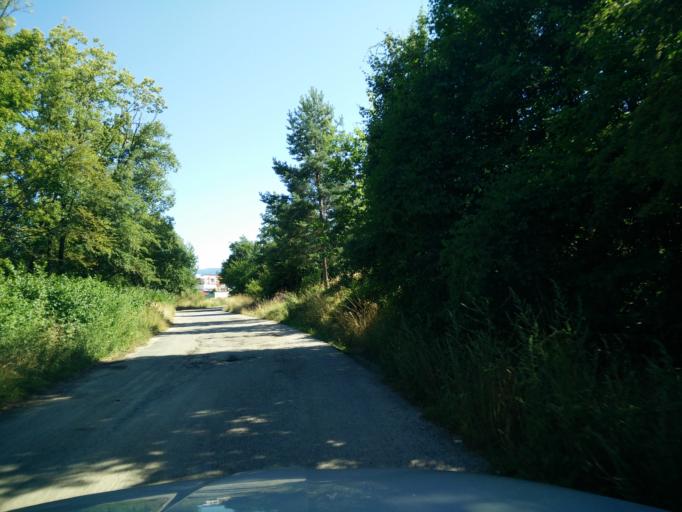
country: SK
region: Nitriansky
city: Bojnice
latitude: 48.7869
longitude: 18.5788
